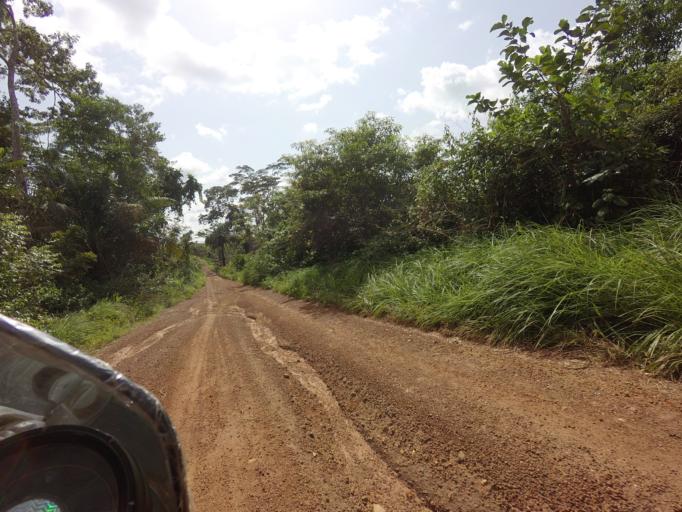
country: SL
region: Eastern Province
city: Daru
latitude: 8.0454
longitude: -10.8471
